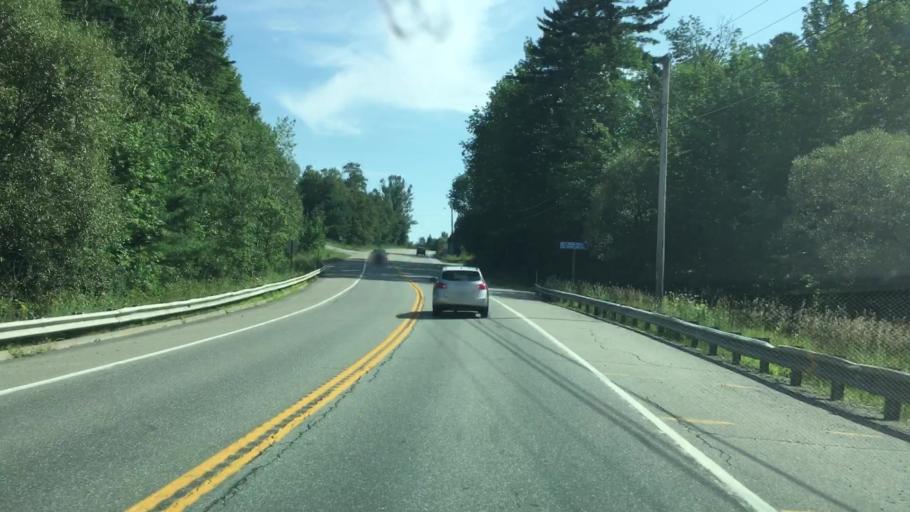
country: US
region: Maine
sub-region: Penobscot County
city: Orrington
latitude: 44.6942
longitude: -68.8479
